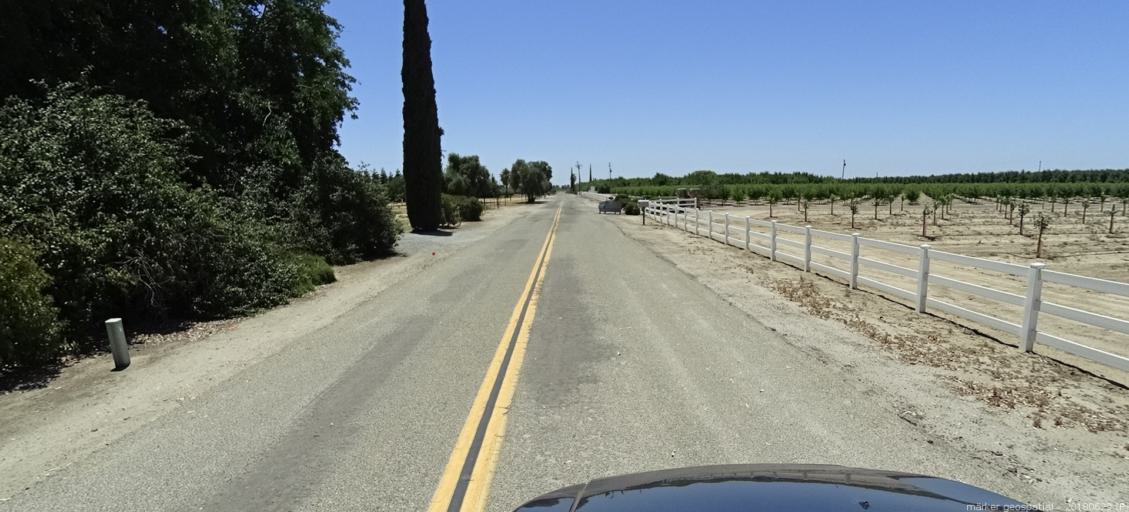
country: US
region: California
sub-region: Madera County
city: Parksdale
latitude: 37.0099
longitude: -119.9912
